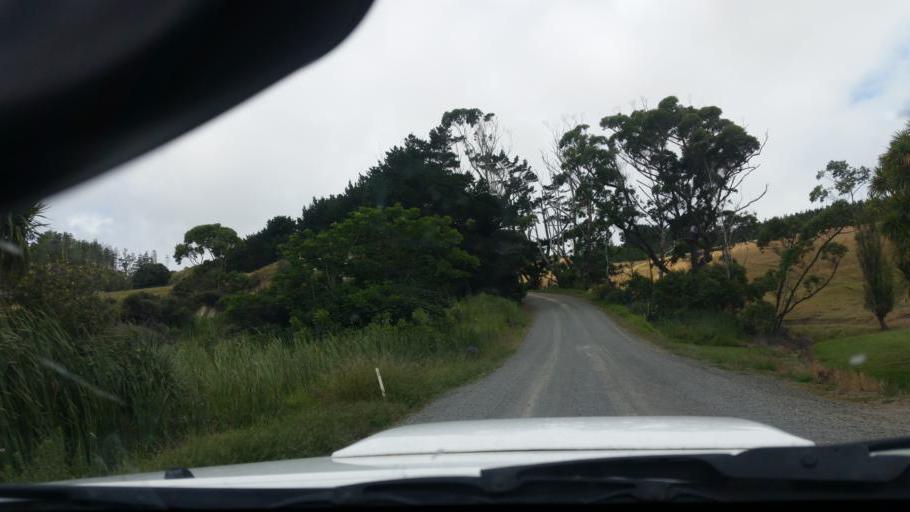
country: NZ
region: Northland
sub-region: Kaipara District
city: Dargaville
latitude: -35.8370
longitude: 173.6608
